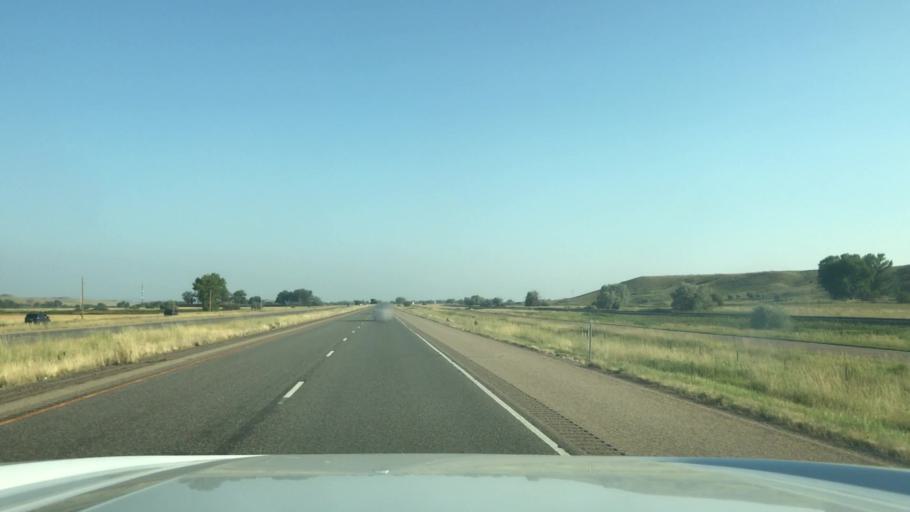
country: US
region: Montana
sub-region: Big Horn County
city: Crow Agency
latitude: 45.6327
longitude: -107.4688
